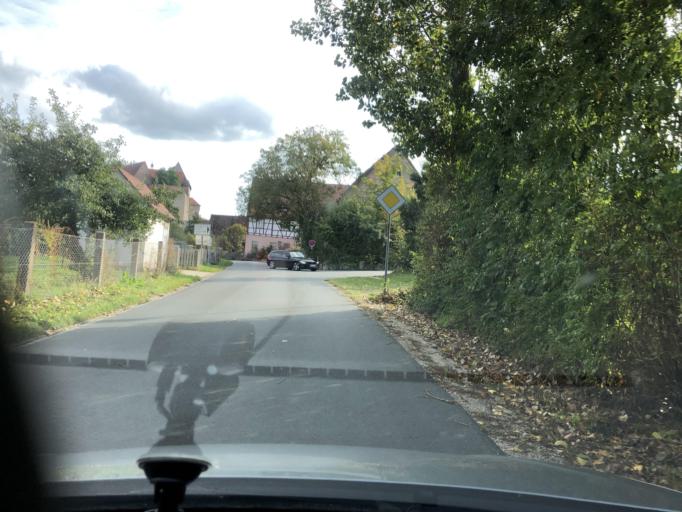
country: DE
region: Bavaria
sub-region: Regierungsbezirk Mittelfranken
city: Cadolzburg
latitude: 49.4629
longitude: 10.8490
